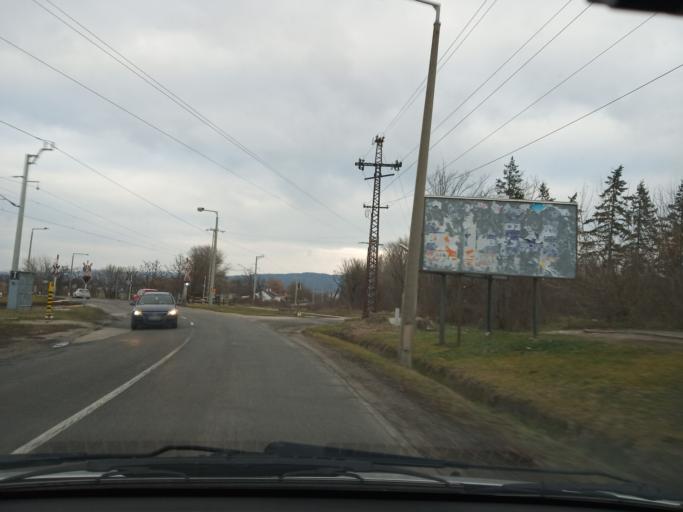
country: HU
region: Komarom-Esztergom
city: Dorog
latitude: 47.7533
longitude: 18.7329
